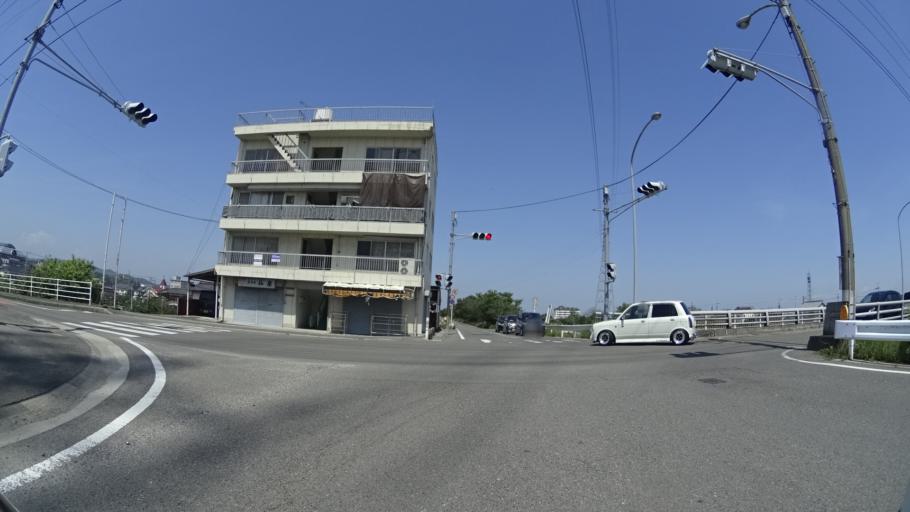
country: JP
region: Ehime
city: Hojo
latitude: 34.0391
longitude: 132.9770
